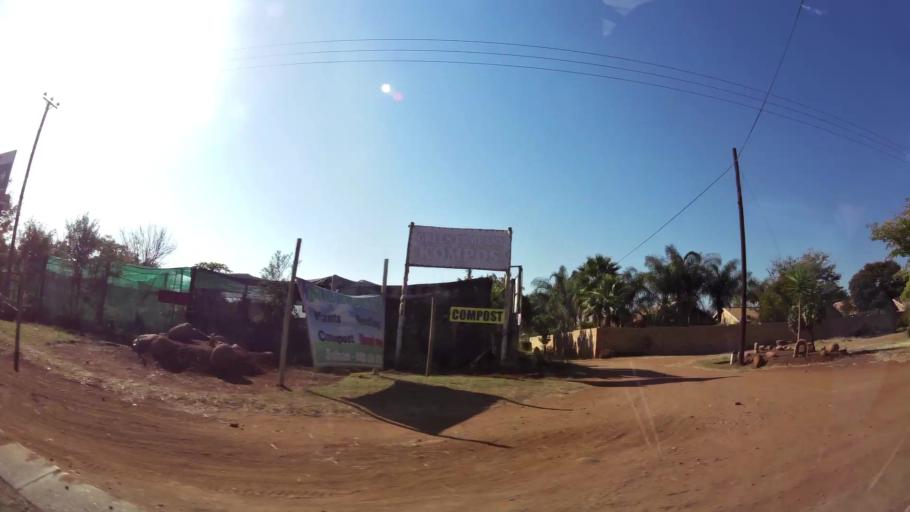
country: ZA
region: Gauteng
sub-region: City of Tshwane Metropolitan Municipality
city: Pretoria
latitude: -25.6716
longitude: 28.2434
